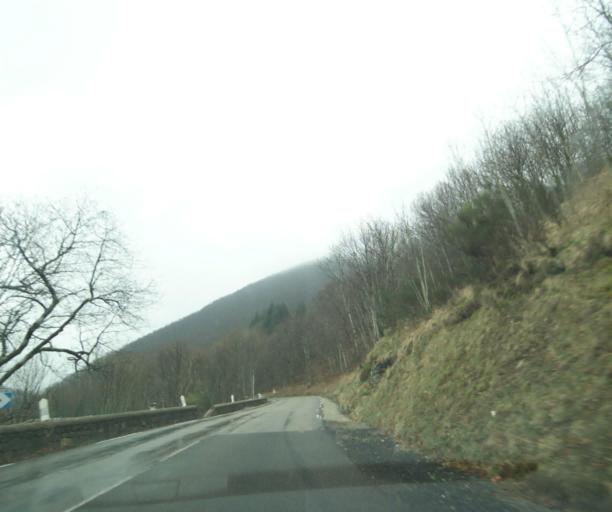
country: FR
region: Rhone-Alpes
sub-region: Departement de l'Ardeche
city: Thueyts
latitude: 44.6647
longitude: 4.1337
